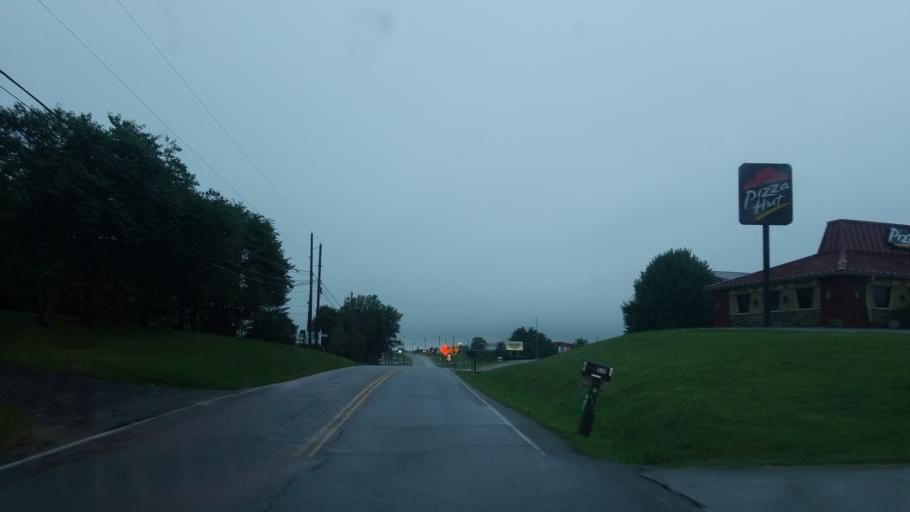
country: US
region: Kentucky
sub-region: Fleming County
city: Flemingsburg
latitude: 38.4153
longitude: -83.7378
